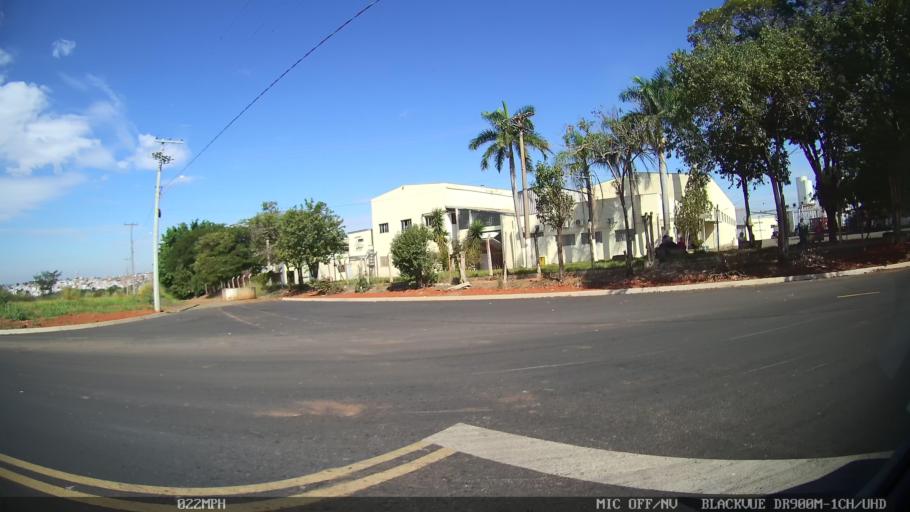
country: BR
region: Sao Paulo
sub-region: Santa Barbara D'Oeste
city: Santa Barbara d'Oeste
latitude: -22.7263
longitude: -47.4077
